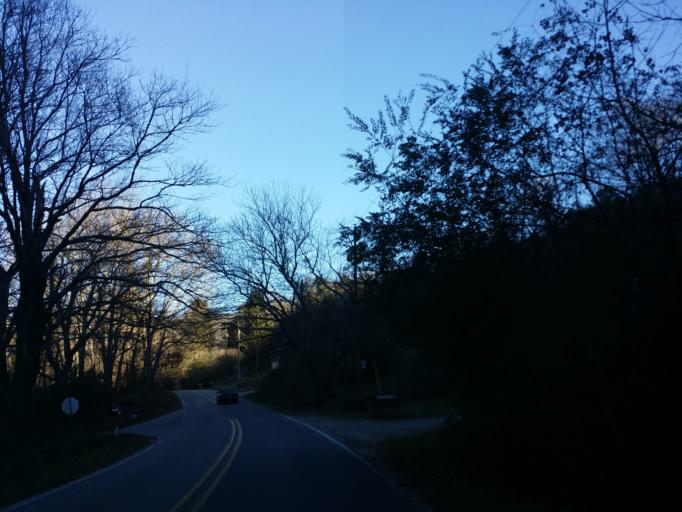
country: US
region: North Carolina
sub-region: Buncombe County
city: Swannanoa
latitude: 35.6331
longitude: -82.4189
